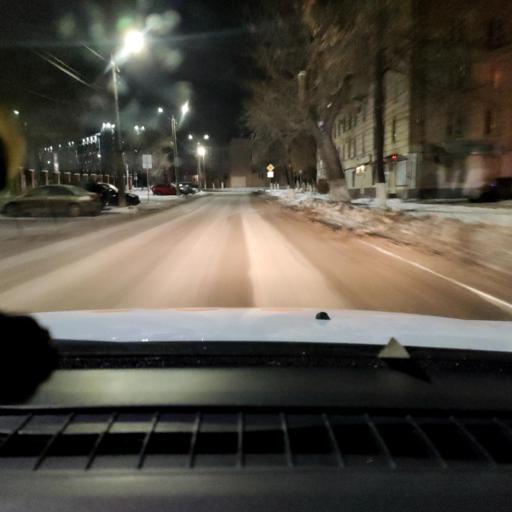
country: RU
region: Samara
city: Novokuybyshevsk
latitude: 53.0977
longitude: 49.9518
